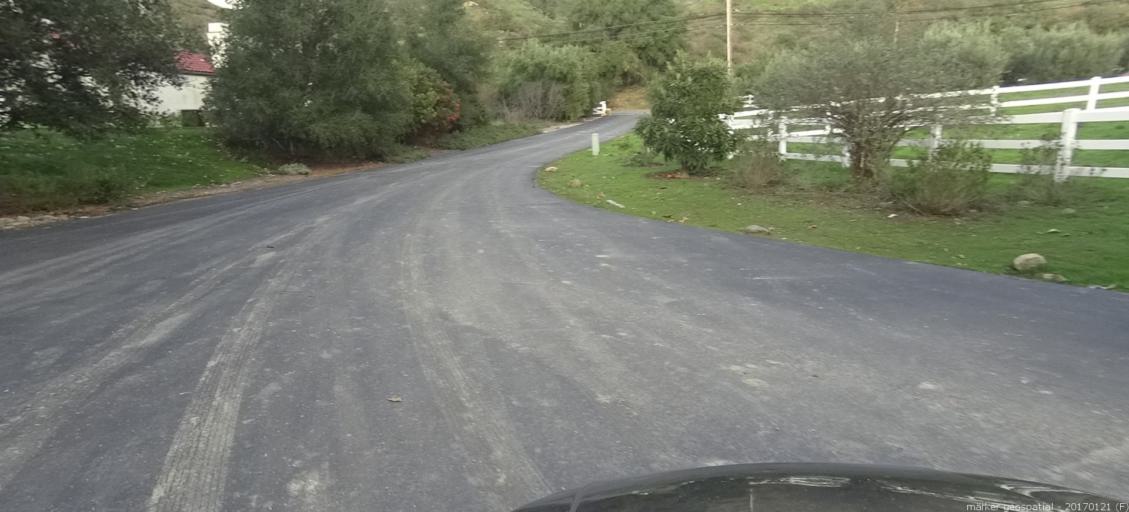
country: US
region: California
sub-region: Orange County
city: Foothill Ranch
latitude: 33.7105
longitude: -117.6409
